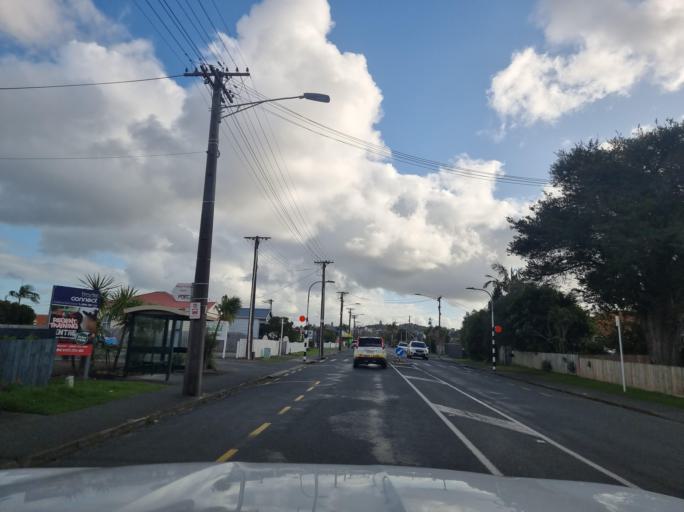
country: NZ
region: Northland
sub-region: Whangarei
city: Whangarei
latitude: -35.7298
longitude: 174.3141
